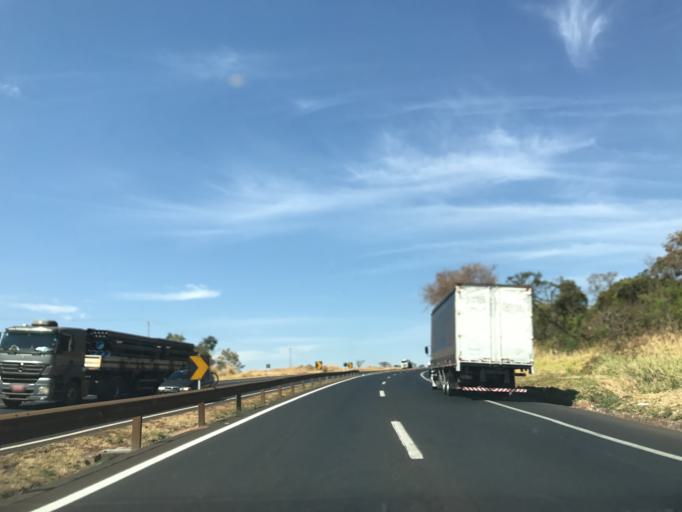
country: BR
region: Minas Gerais
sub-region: Monte Alegre De Minas
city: Monte Alegre de Minas
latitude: -18.8001
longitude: -49.0814
